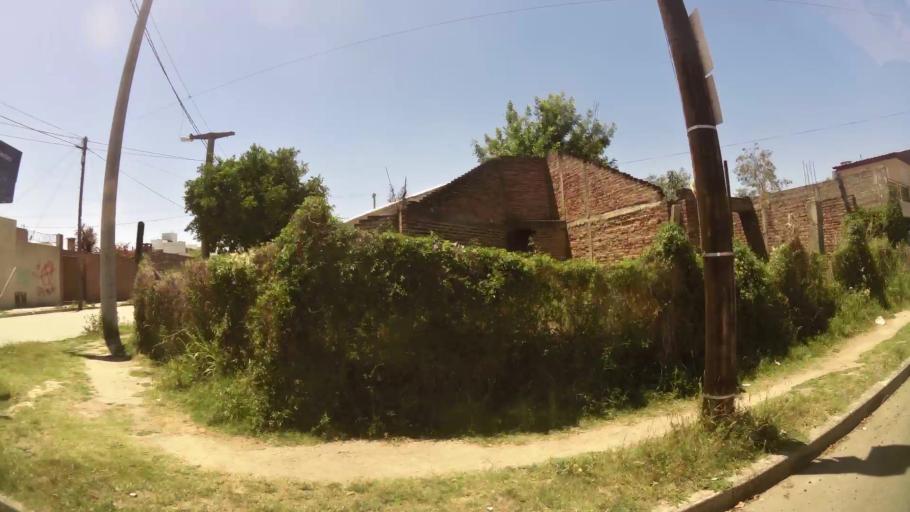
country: AR
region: Cordoba
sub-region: Departamento de Capital
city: Cordoba
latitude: -31.4288
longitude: -64.1272
